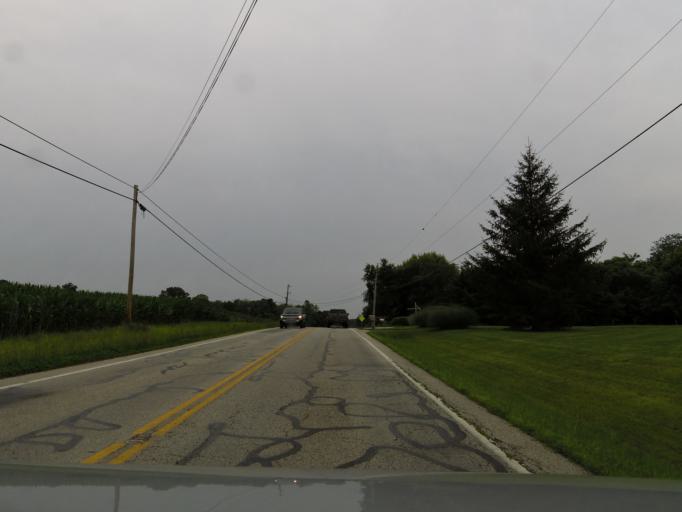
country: US
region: Ohio
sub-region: Clinton County
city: Wilmington
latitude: 39.4726
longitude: -83.8878
